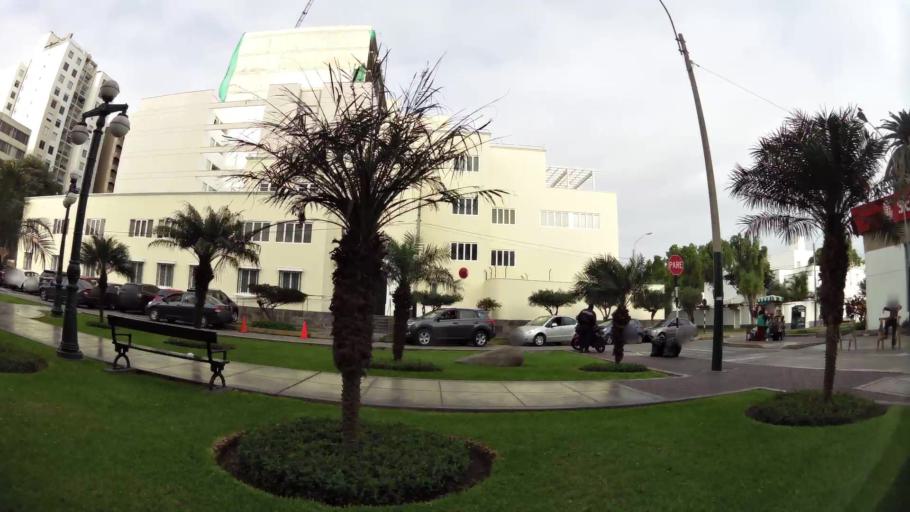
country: PE
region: Lima
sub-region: Lima
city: San Isidro
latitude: -12.0971
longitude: -77.0587
